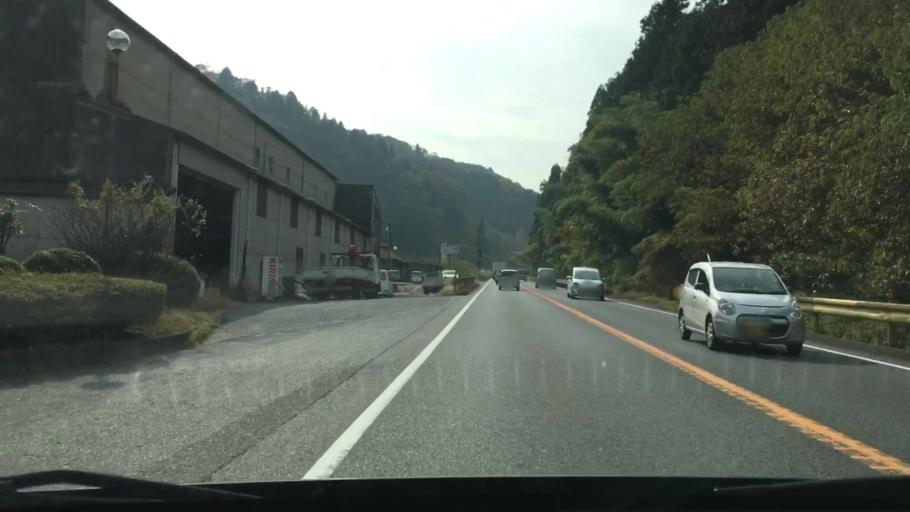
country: JP
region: Yamaguchi
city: Iwakuni
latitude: 34.1268
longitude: 132.1384
